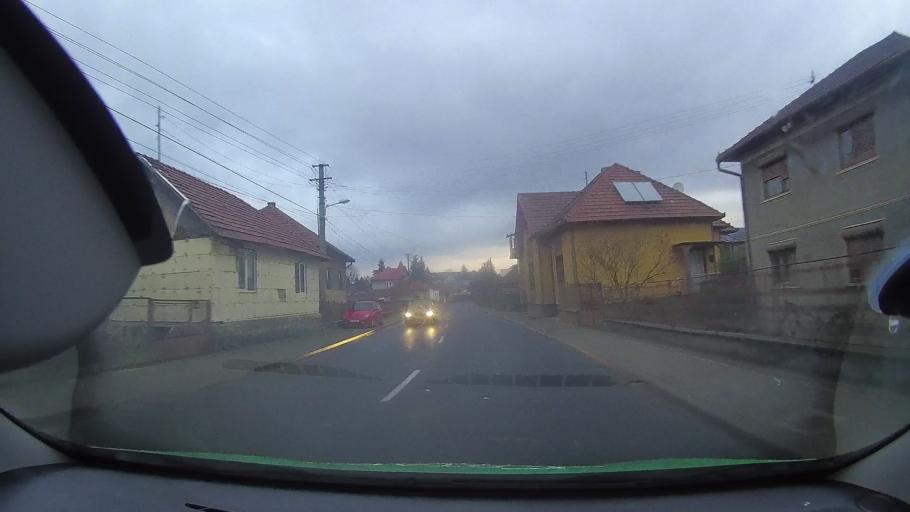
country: RO
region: Hunedoara
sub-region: Municipiul Brad
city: Brad
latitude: 46.1335
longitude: 22.7835
